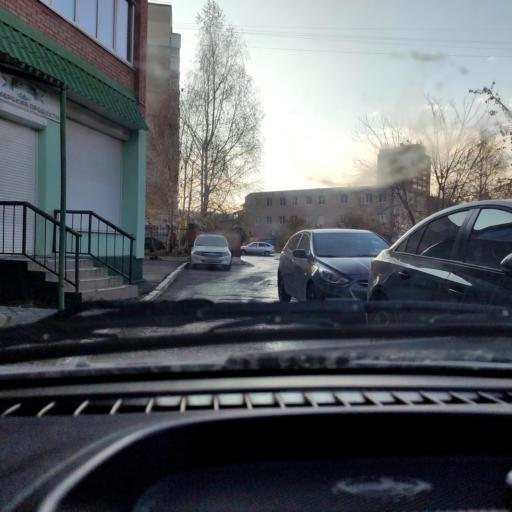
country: RU
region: Samara
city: Tol'yatti
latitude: 53.5429
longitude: 49.3417
